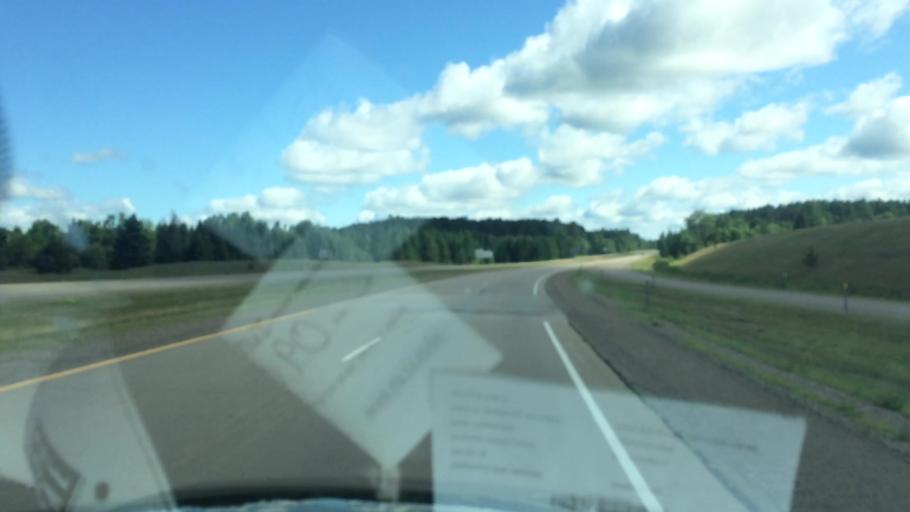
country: US
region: Wisconsin
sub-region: Lincoln County
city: Tomahawk
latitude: 45.4986
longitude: -89.6950
